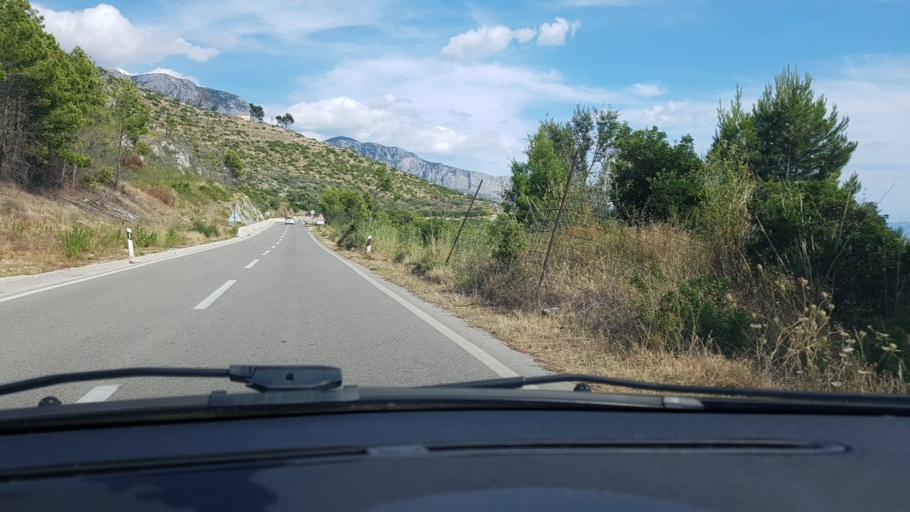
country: HR
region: Splitsko-Dalmatinska
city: Tucepi
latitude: 43.2809
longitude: 17.0439
